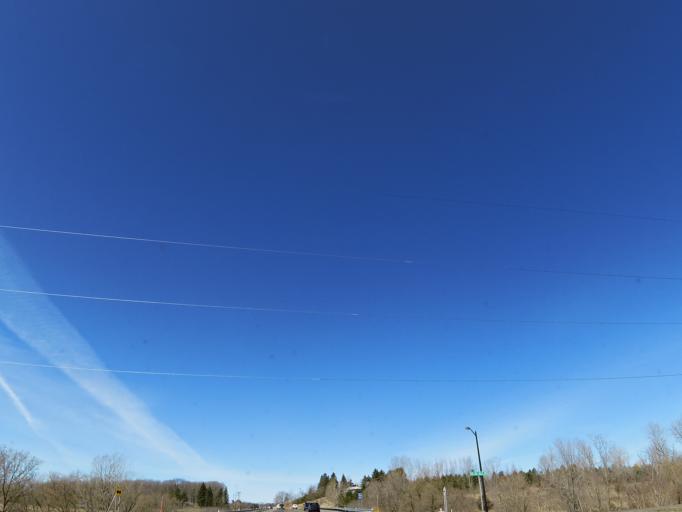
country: US
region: Minnesota
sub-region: Hennepin County
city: Medina
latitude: 45.0644
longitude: -93.6046
